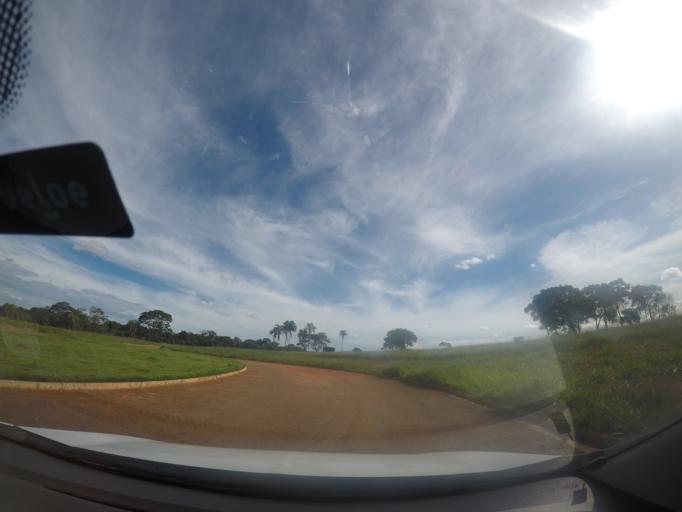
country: BR
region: Goias
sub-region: Inhumas
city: Inhumas
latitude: -16.4030
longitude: -49.4698
